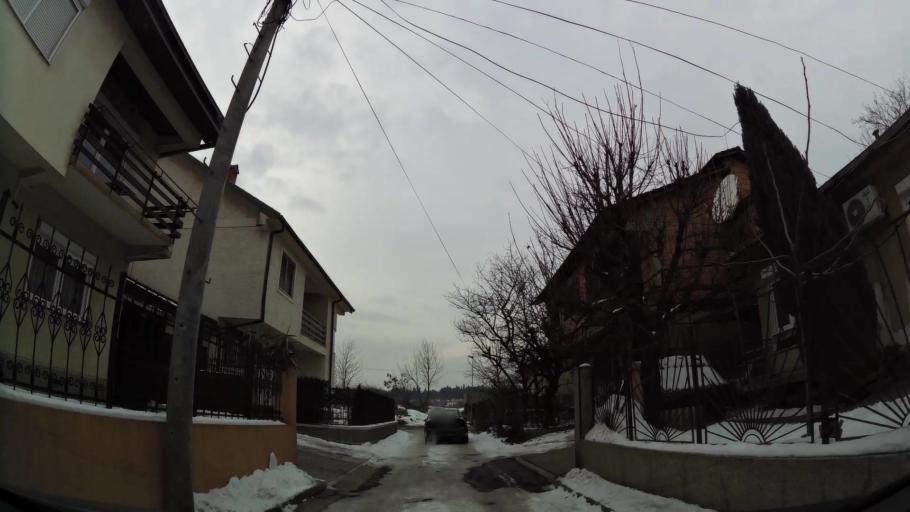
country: MK
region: Butel
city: Butel
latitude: 42.0328
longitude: 21.4409
